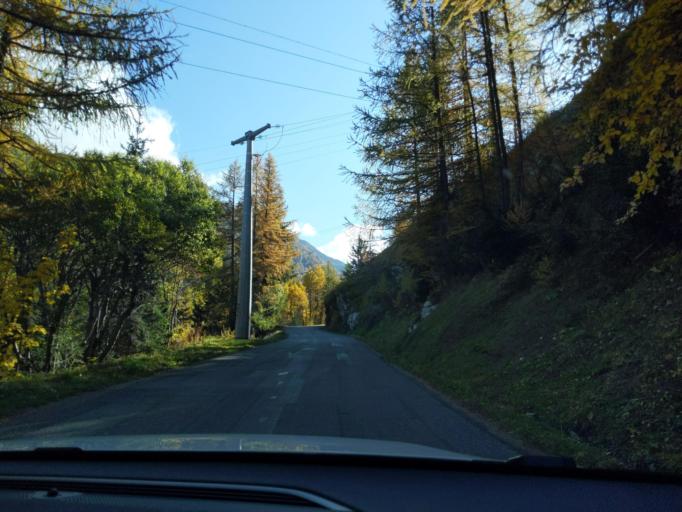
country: FR
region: Rhone-Alpes
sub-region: Departement de la Savoie
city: Tignes
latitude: 45.5026
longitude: 6.9216
